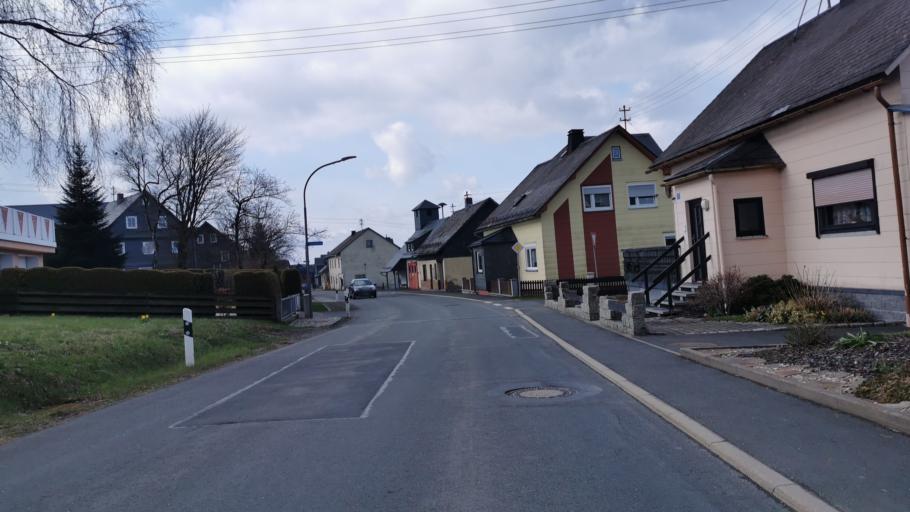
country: DE
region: Bavaria
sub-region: Upper Franconia
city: Tettau
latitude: 50.4463
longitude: 11.3166
